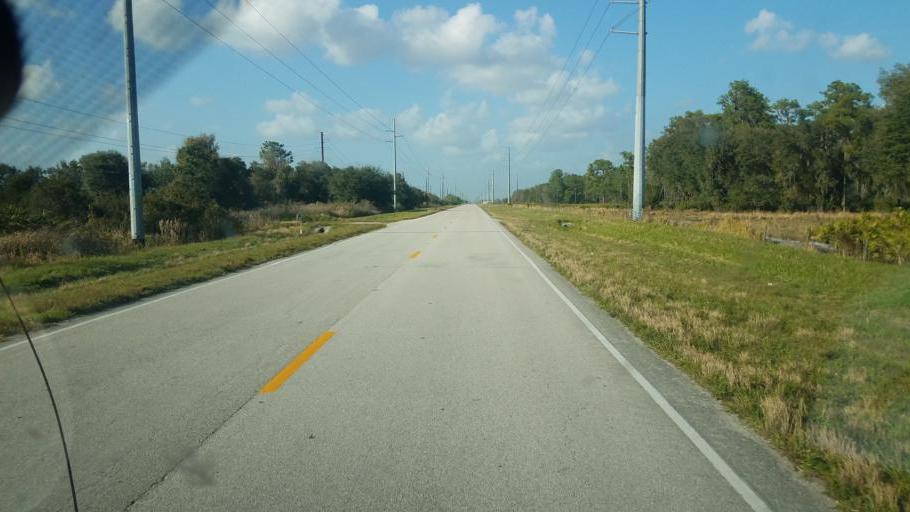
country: US
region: Florida
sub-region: Hardee County
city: Wauchula
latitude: 27.5144
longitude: -81.9251
